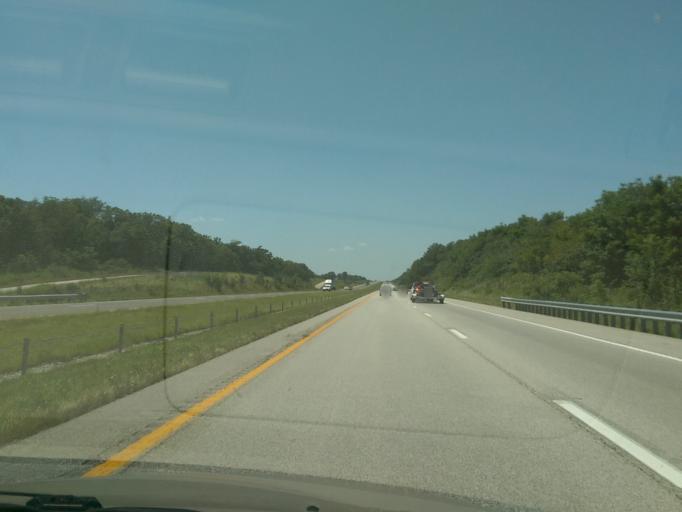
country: US
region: Missouri
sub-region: Saline County
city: Marshall
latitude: 38.9500
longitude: -93.0404
